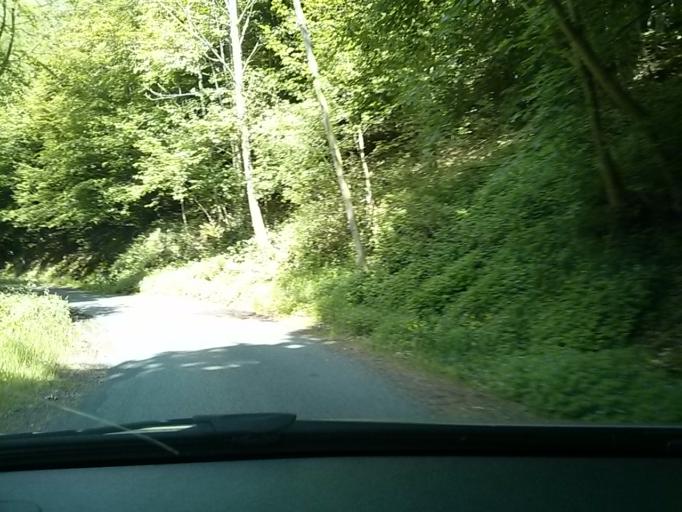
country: FR
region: Rhone-Alpes
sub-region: Departement de la Loire
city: Saint-Chamond
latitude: 45.3975
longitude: 4.5516
